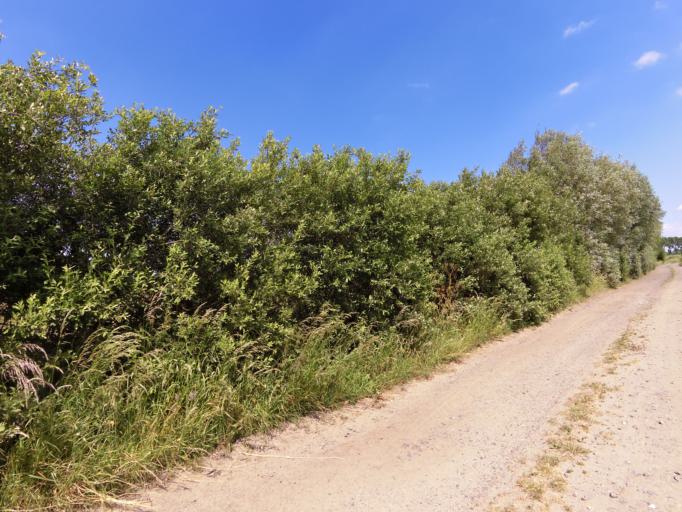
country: BE
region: Flanders
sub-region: Provincie West-Vlaanderen
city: Oudenburg
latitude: 51.1497
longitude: 3.0119
